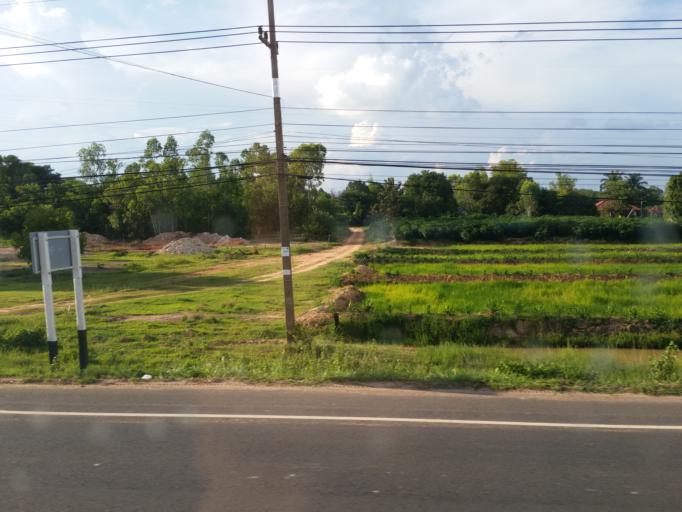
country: TH
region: Changwat Ubon Ratchathani
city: Sirindhorn
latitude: 15.2013
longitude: 105.3745
